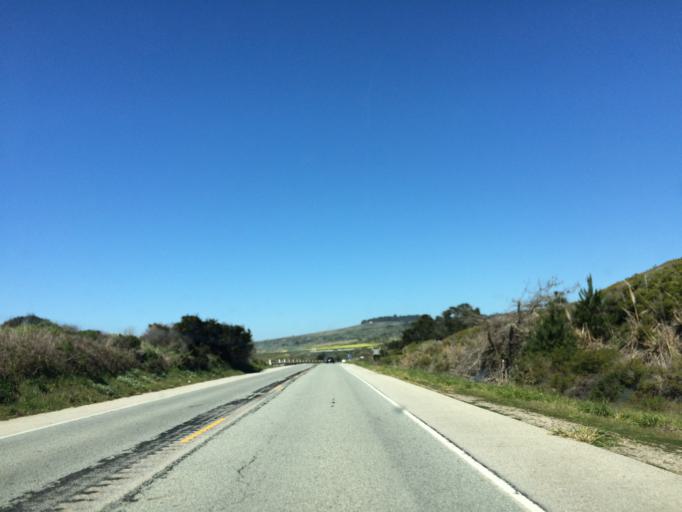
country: US
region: California
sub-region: Santa Cruz County
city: Boulder Creek
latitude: 37.1617
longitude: -122.3583
